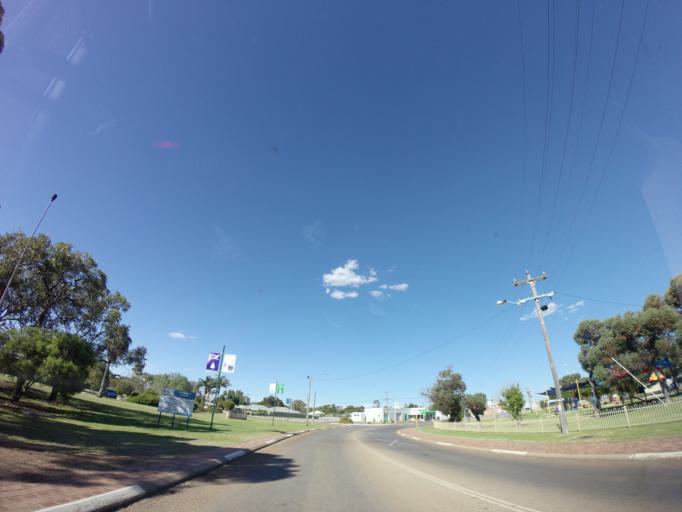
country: AU
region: Western Australia
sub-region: Merredin
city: Merredin
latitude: -31.4818
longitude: 118.2726
